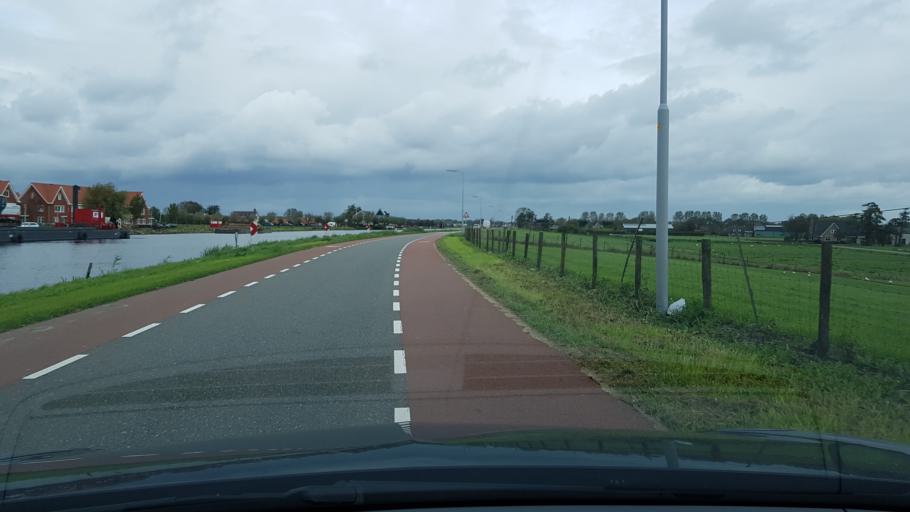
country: NL
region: South Holland
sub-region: Gemeente Hillegom
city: Hillegom
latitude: 52.2953
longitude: 4.5975
